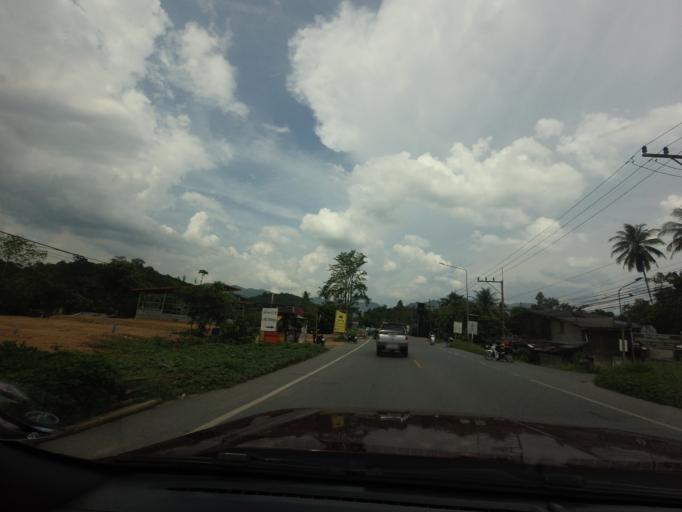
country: TH
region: Yala
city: Ban Nang Sata
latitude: 6.2662
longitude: 101.2674
